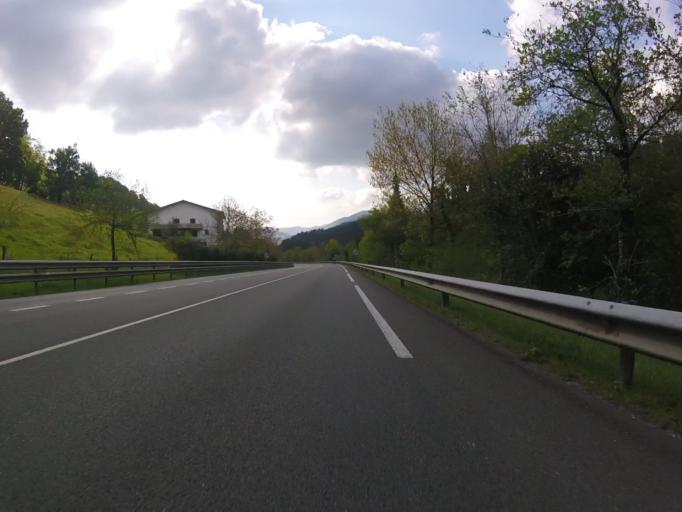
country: ES
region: Basque Country
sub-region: Provincia de Guipuzcoa
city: Azkoitia
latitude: 43.1945
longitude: -2.3363
